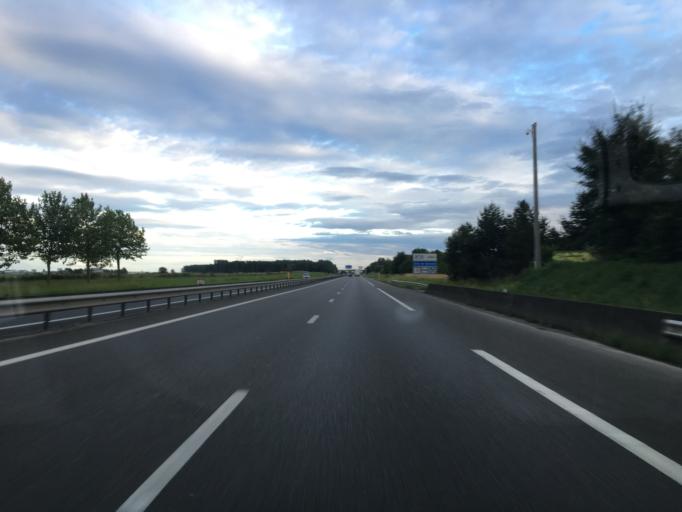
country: FR
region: Ile-de-France
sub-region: Departement de Seine-et-Marne
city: Moissy-Cramayel
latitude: 48.6211
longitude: 2.6299
